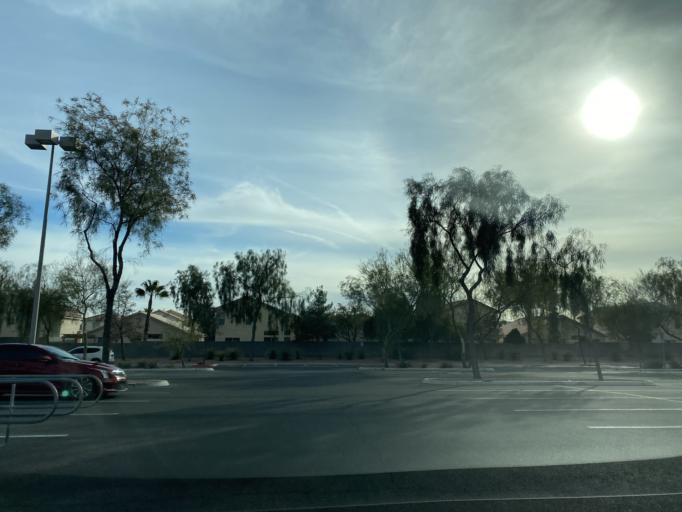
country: US
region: Nevada
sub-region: Clark County
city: North Las Vegas
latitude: 36.2723
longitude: -115.2099
